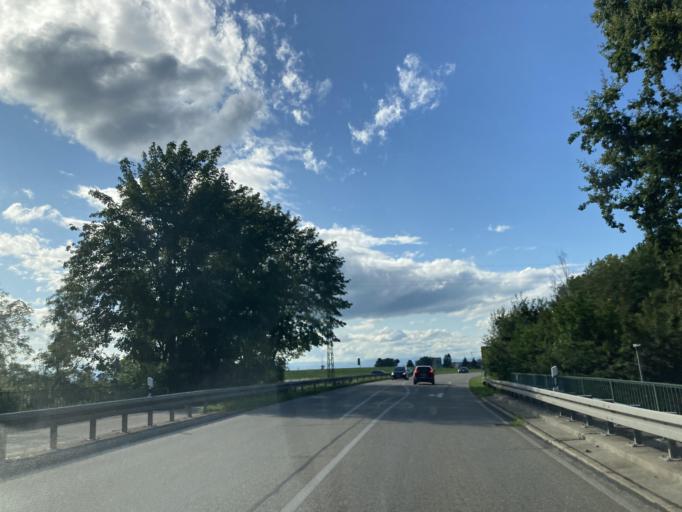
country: DE
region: Baden-Wuerttemberg
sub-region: Freiburg Region
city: Unterkrozingen
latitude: 47.9278
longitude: 7.6916
